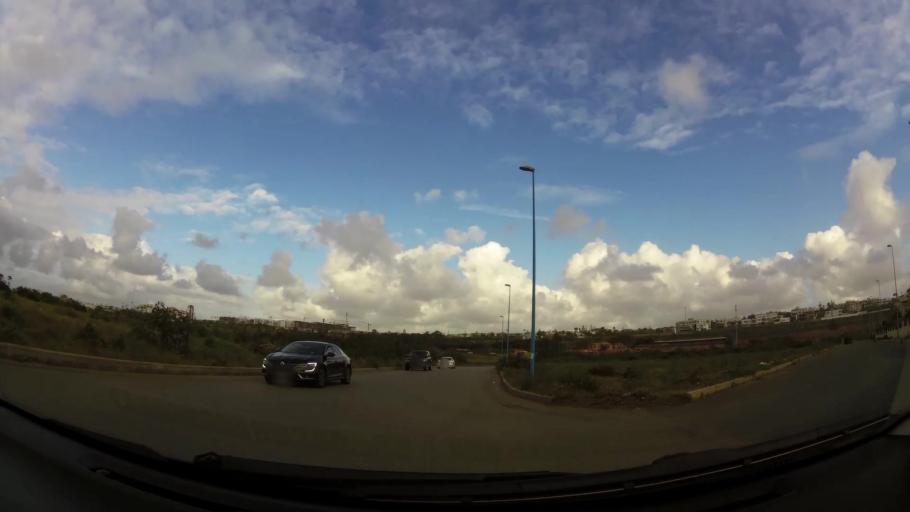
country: MA
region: Grand Casablanca
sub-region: Casablanca
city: Casablanca
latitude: 33.5788
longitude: -7.6925
